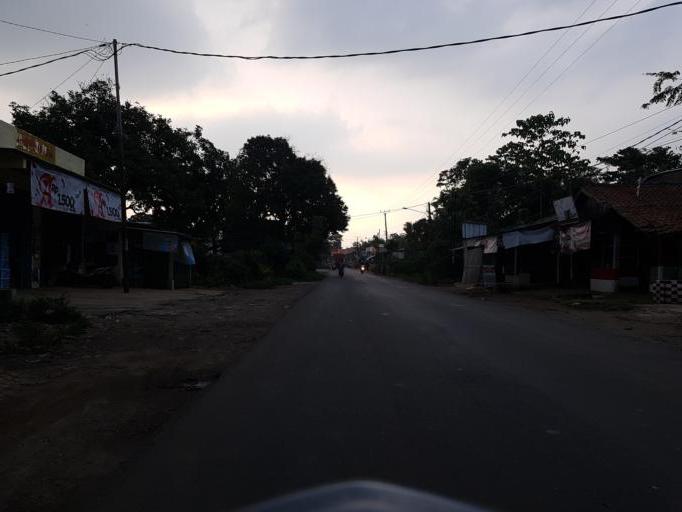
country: ID
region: West Java
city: Parung
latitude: -6.4744
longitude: 106.7239
